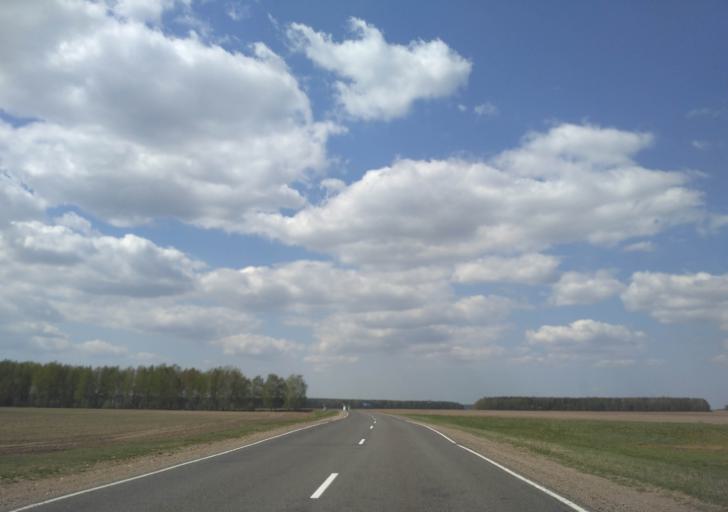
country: BY
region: Minsk
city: Vilyeyka
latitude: 54.5165
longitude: 27.0360
